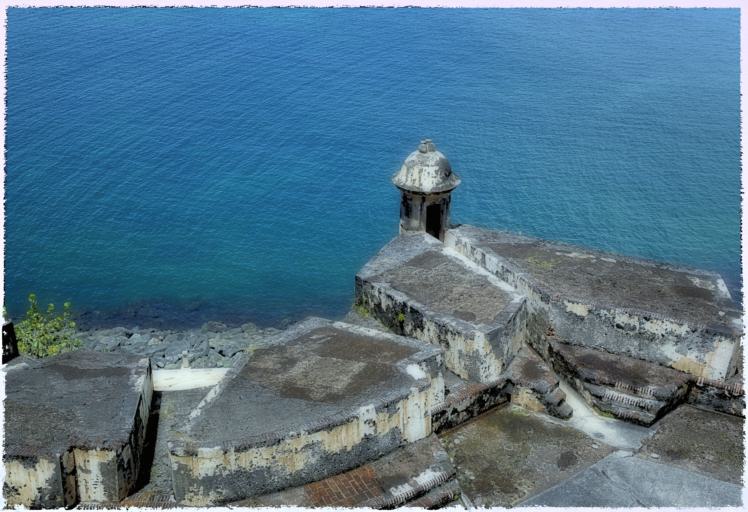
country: PR
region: San Juan
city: San Juan
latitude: 18.4709
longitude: -66.1242
